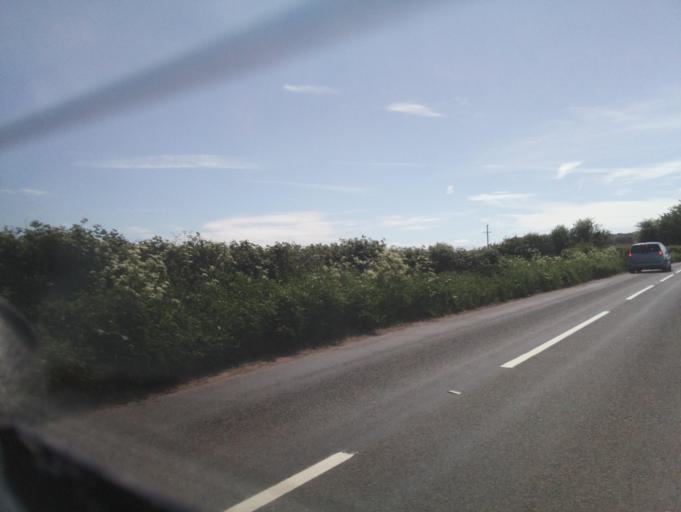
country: GB
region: Wales
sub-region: Monmouthshire
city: Mitchel Troy
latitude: 51.7307
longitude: -2.7504
